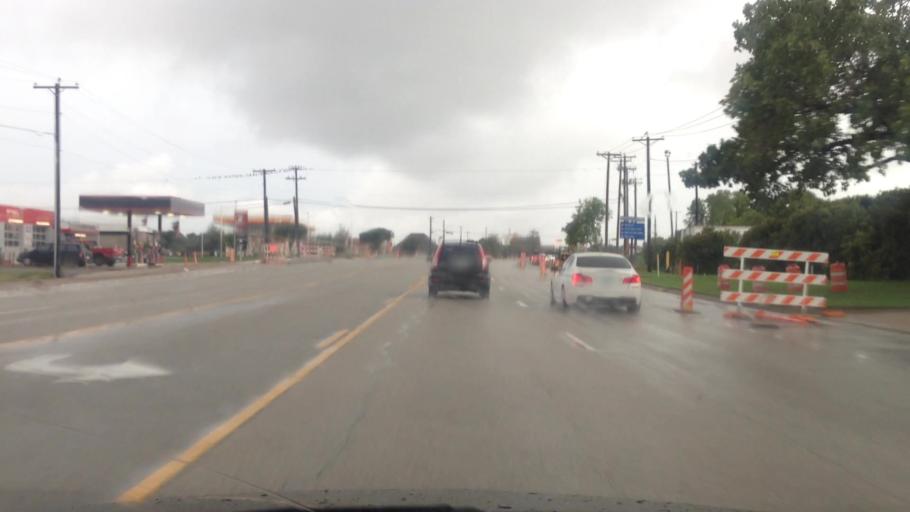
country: US
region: Texas
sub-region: Tarrant County
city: North Richland Hills
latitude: 32.8643
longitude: -97.2088
